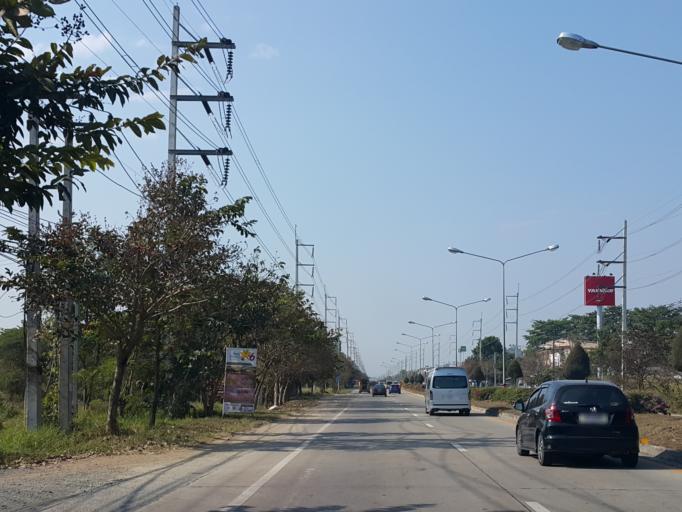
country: TH
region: Chiang Mai
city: San Sai
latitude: 18.8459
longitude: 99.0778
